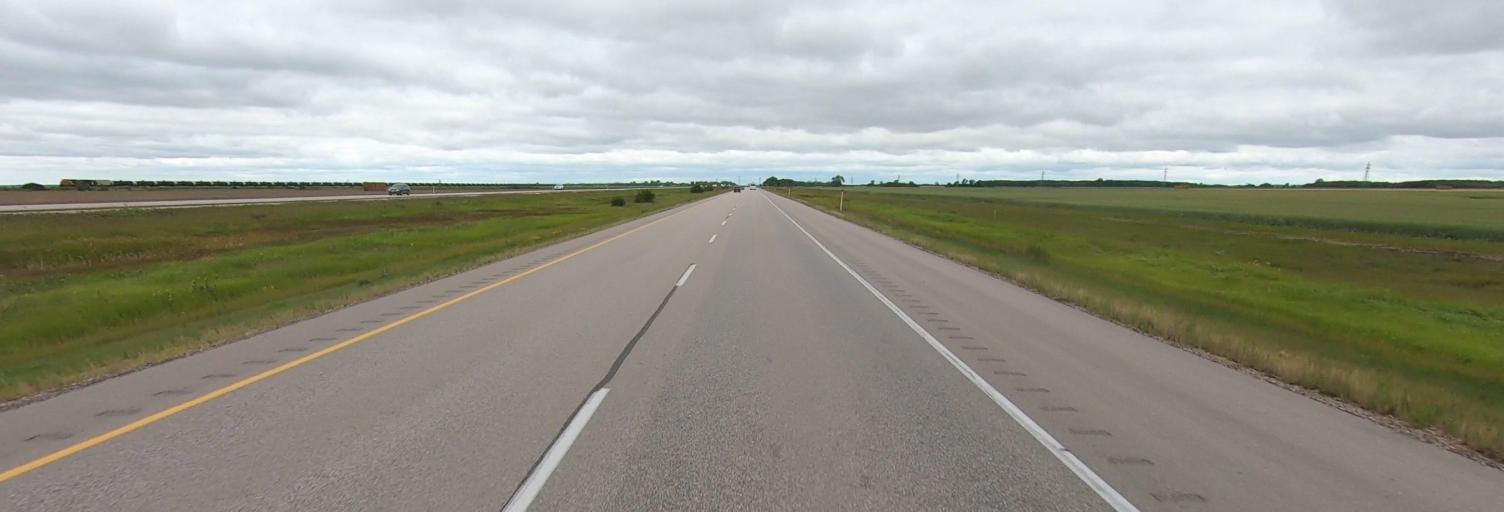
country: CA
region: Manitoba
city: Portage la Prairie
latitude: 49.9260
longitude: -97.8598
